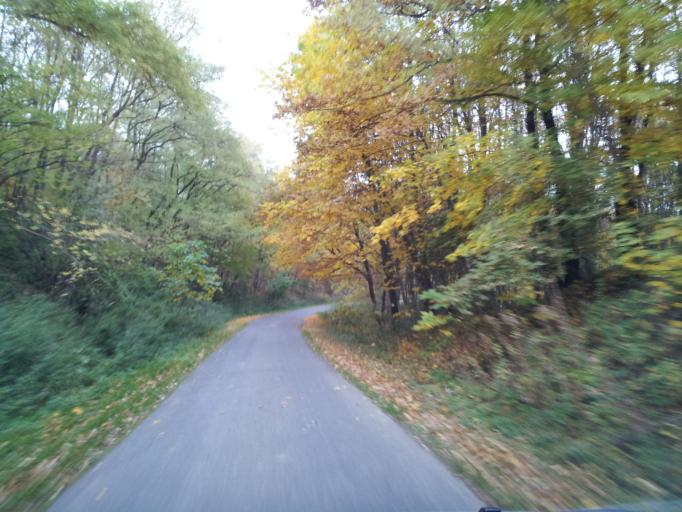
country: HU
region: Gyor-Moson-Sopron
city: Pannonhalma
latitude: 47.4971
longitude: 17.7380
